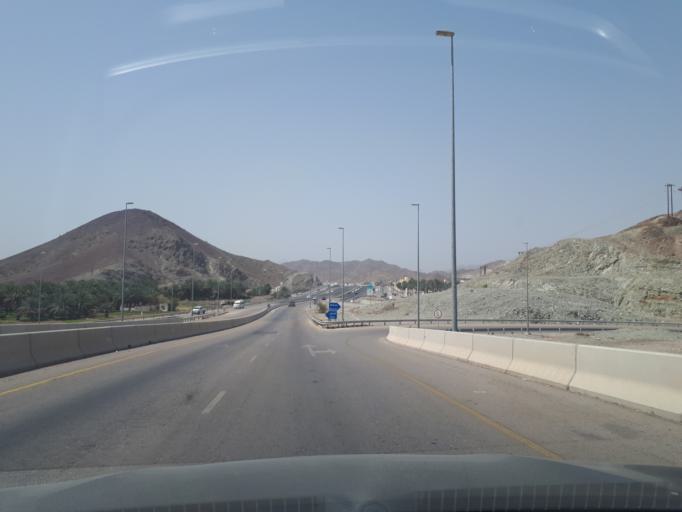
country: OM
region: Muhafazat ad Dakhiliyah
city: Bidbid
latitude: 23.4131
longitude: 58.1021
